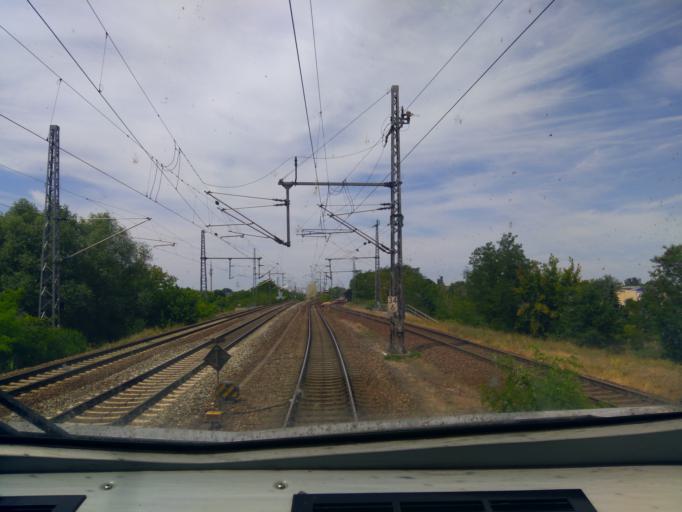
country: DE
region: Brandenburg
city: Nauen
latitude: 52.6098
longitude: 12.8965
